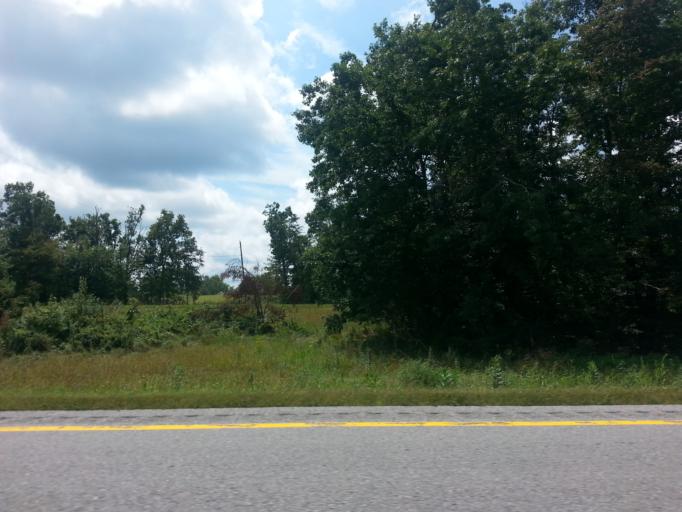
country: US
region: Tennessee
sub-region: Putnam County
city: Monterey
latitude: 36.0520
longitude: -85.1622
